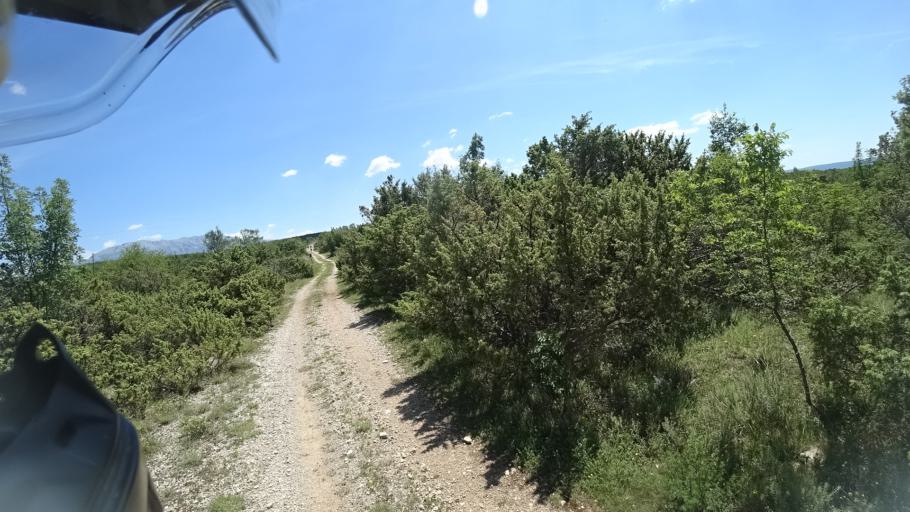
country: HR
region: Sibensko-Kniniska
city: Knin
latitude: 44.0326
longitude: 16.2351
